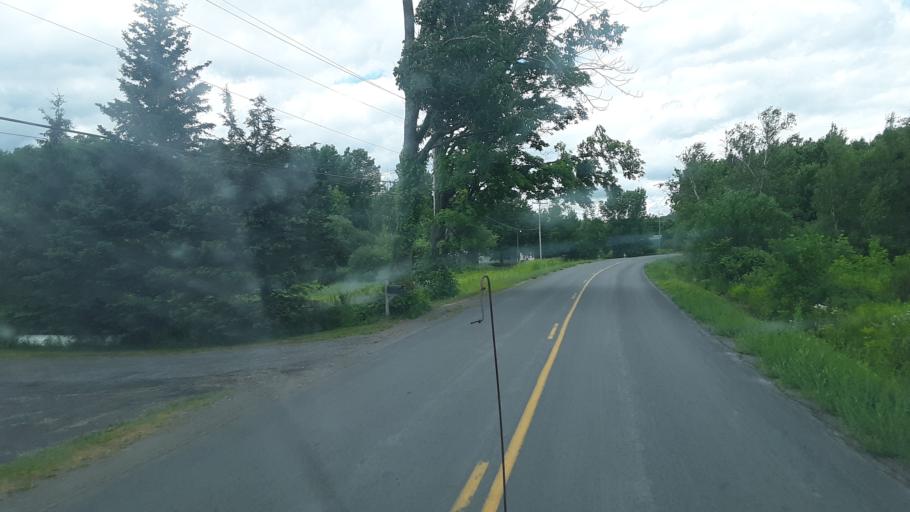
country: US
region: New York
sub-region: Oneida County
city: Rome
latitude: 43.3462
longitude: -75.5542
